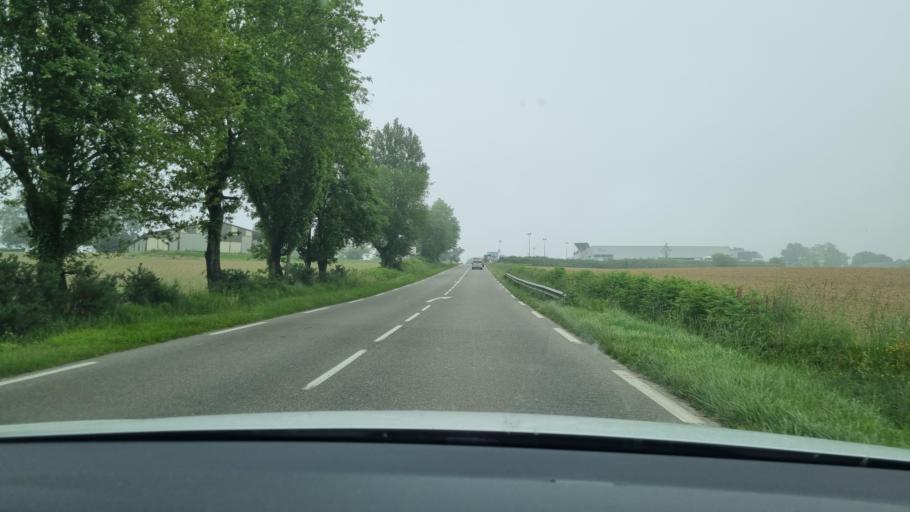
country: FR
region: Aquitaine
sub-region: Departement des Landes
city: Hagetmau
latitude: 43.6337
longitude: -0.6179
